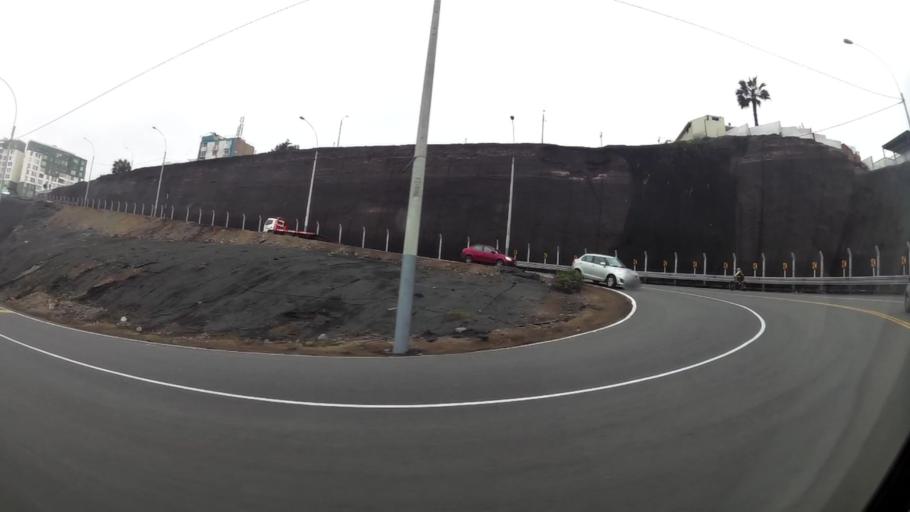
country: PE
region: Lima
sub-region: Lima
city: San Isidro
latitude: -12.0919
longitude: -77.0836
